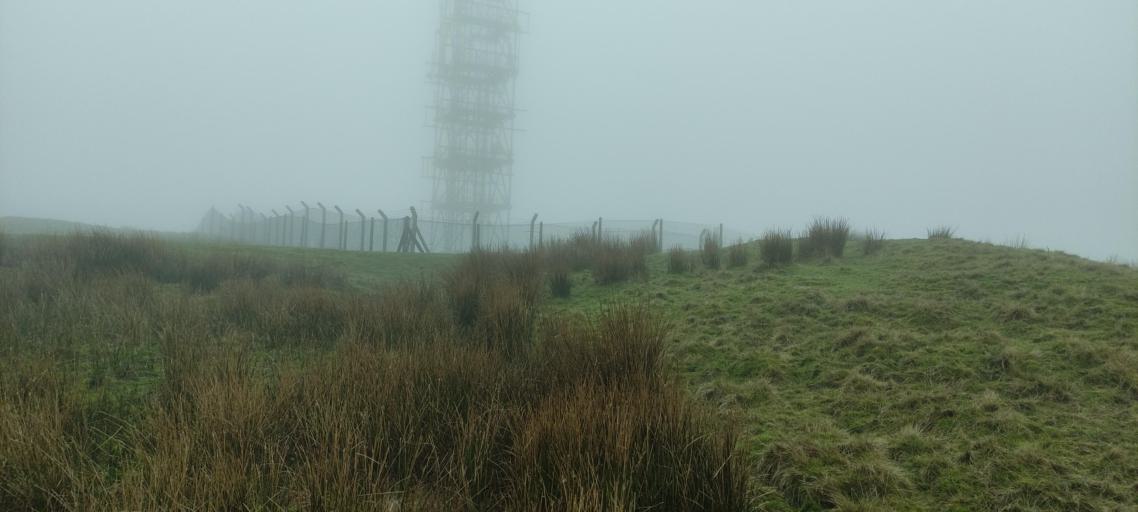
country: GB
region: England
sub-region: Cumbria
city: Kendal
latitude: 54.3968
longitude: -2.6379
